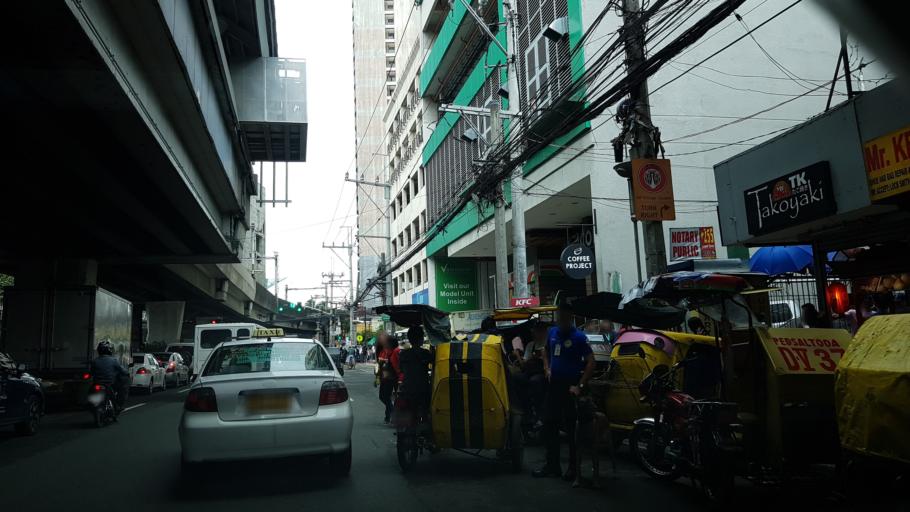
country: PH
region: Metro Manila
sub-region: City of Manila
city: Port Area
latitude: 14.5634
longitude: 120.9949
